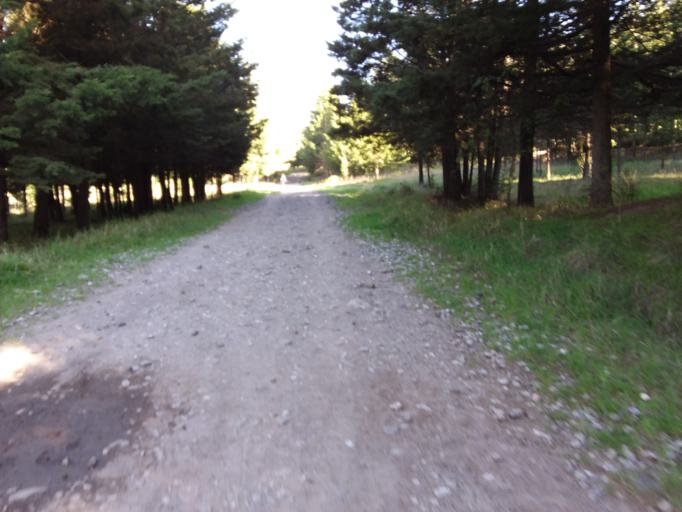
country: MX
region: Mexico
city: San Marcos Yachihuacaltepec
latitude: 19.3129
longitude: -99.6947
